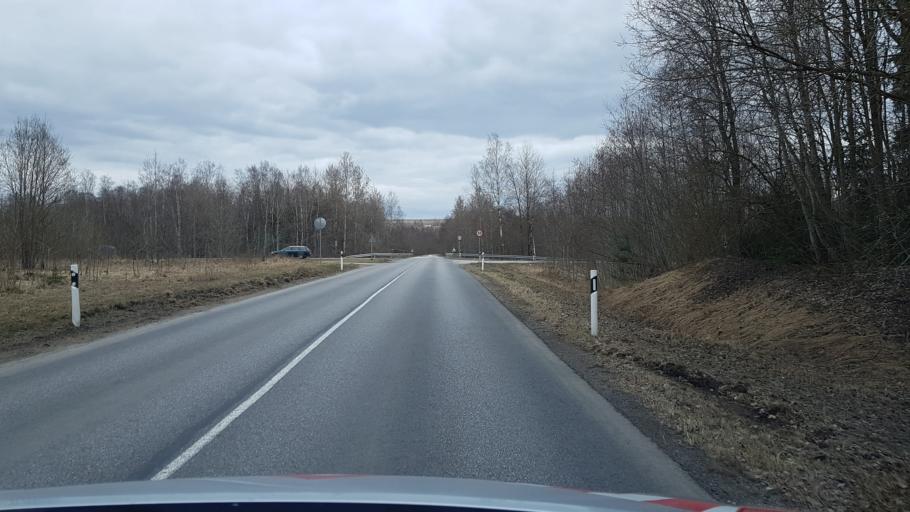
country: EE
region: Ida-Virumaa
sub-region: Narva linn
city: Narva
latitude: 59.3527
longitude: 28.0958
